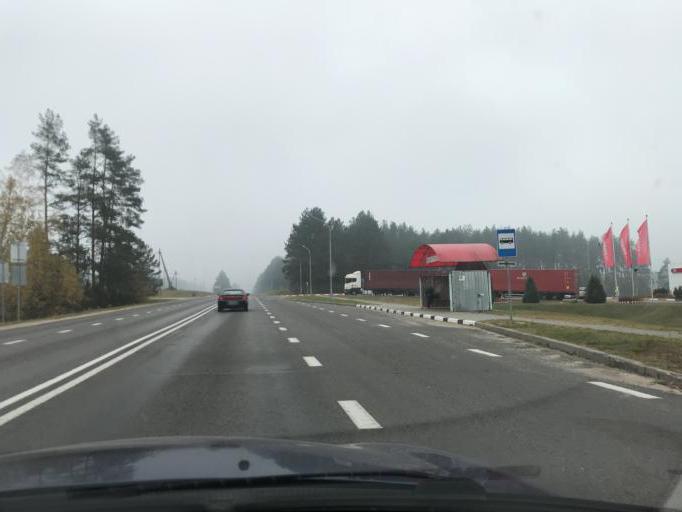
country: BY
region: Grodnenskaya
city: Hrodna
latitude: 53.8059
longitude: 23.8607
